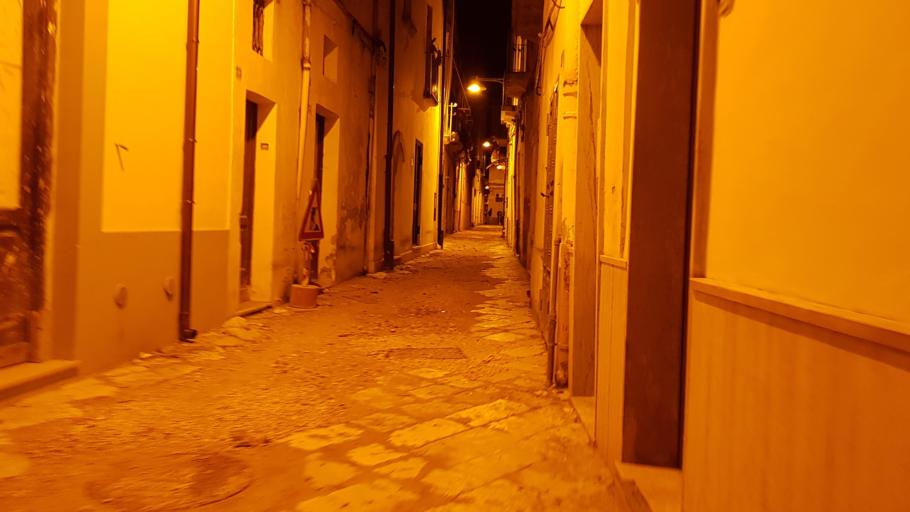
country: IT
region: Apulia
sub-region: Provincia di Brindisi
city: Brindisi
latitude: 40.6385
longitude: 17.9426
